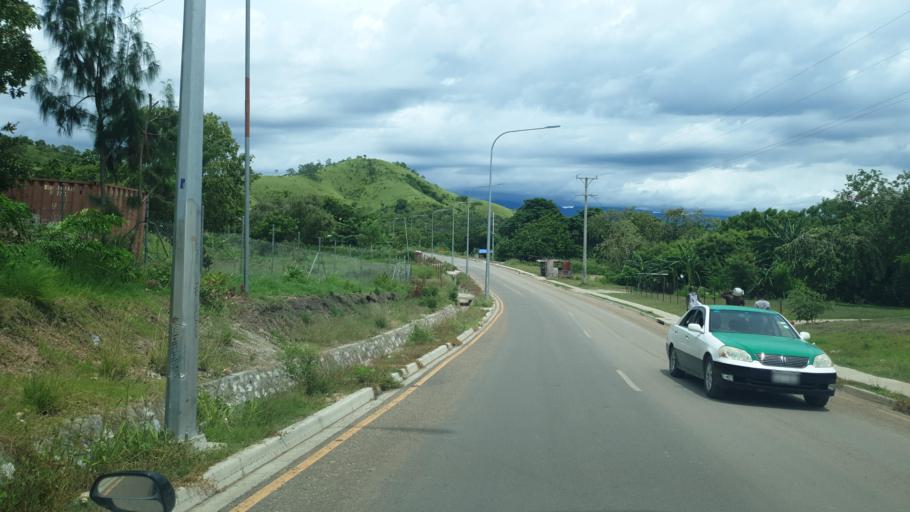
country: PG
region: National Capital
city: Port Moresby
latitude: -9.5289
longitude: 147.2450
